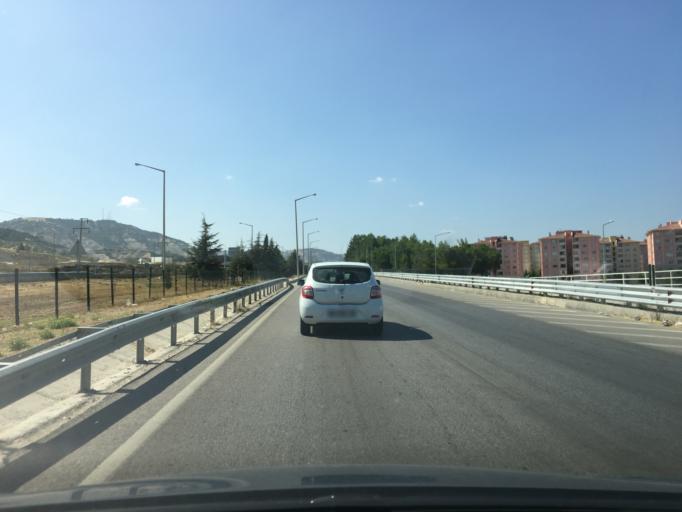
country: TR
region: Burdur
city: Burdur
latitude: 37.7378
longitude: 30.3115
